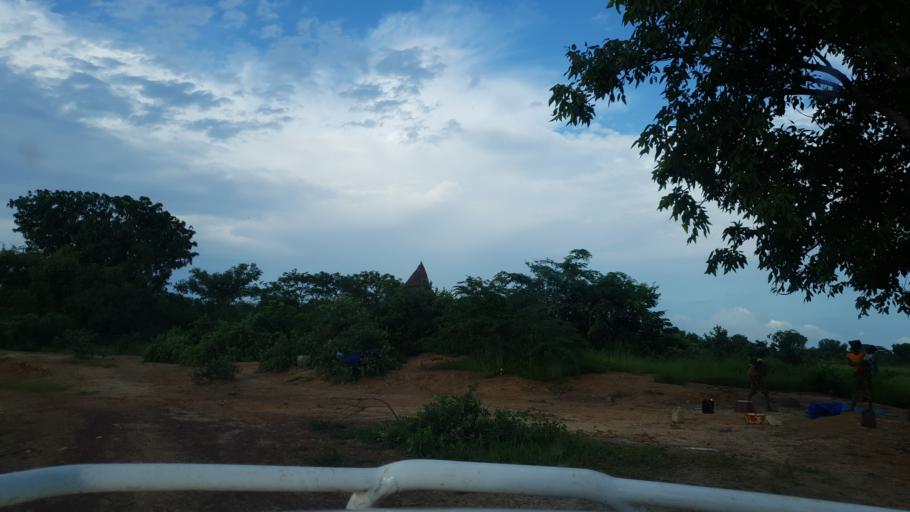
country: ML
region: Sikasso
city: Kolondieba
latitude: 11.5740
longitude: -6.6909
